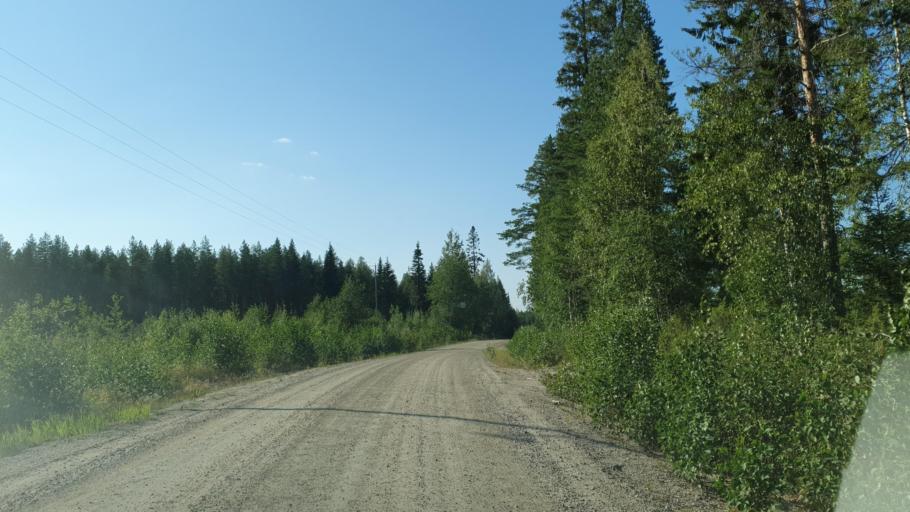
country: FI
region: Kainuu
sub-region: Kehys-Kainuu
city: Kuhmo
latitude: 64.0329
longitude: 29.6822
